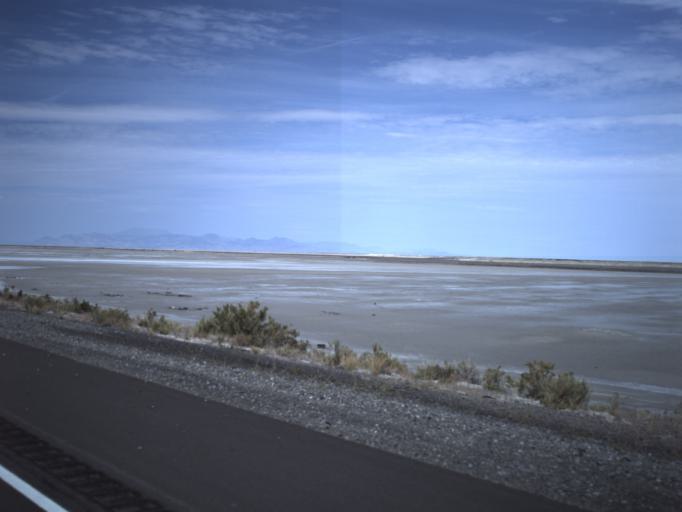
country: US
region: Utah
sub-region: Tooele County
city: Wendover
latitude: 40.7281
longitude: -113.2973
